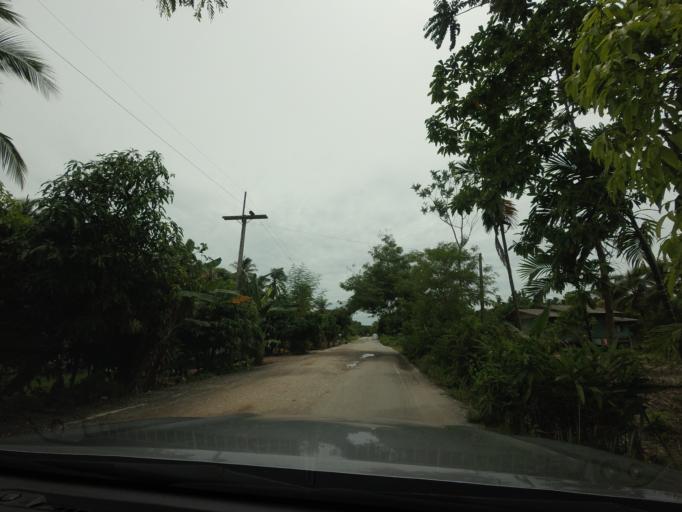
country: TH
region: Pattani
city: Sai Buri
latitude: 6.6588
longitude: 101.5524
